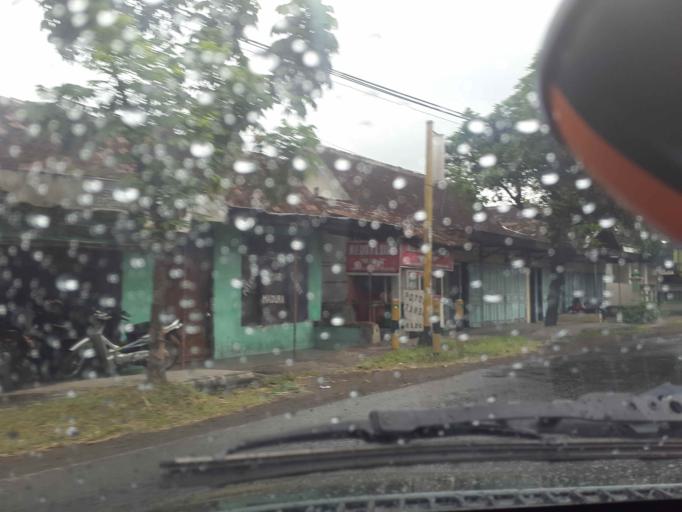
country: ID
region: Central Java
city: Sragen
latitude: -7.4325
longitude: 111.0340
